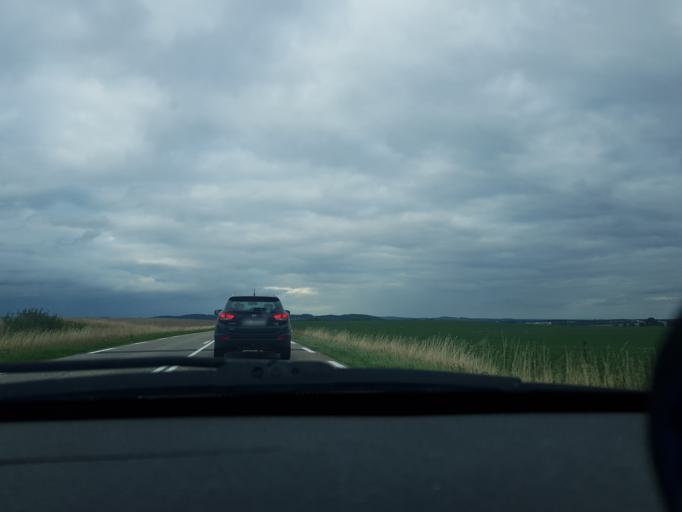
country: FR
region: Lorraine
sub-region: Departement de la Moselle
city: Morhange
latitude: 48.9284
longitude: 6.6005
